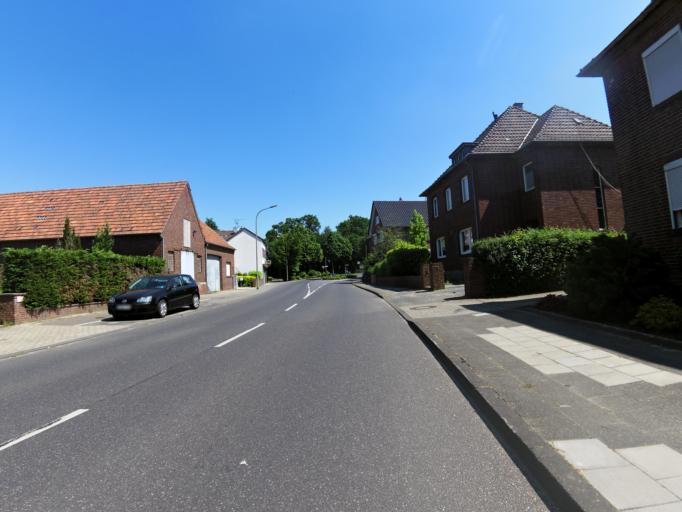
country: DE
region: North Rhine-Westphalia
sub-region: Regierungsbezirk Koln
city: Gangelt
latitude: 50.9886
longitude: 5.9941
